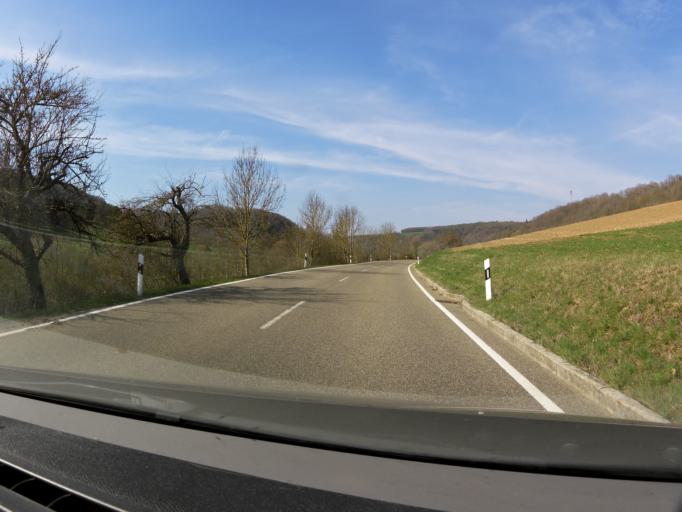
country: DE
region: Bavaria
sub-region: Regierungsbezirk Mittelfranken
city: Adelshofen
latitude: 49.4286
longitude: 10.1438
